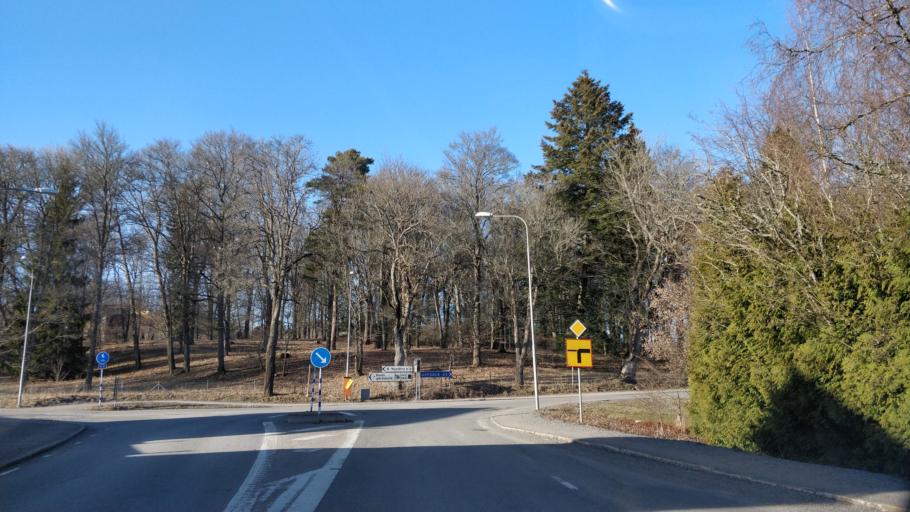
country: SE
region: Uppsala
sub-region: Enkopings Kommun
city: Orsundsbro
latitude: 59.7382
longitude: 17.3104
